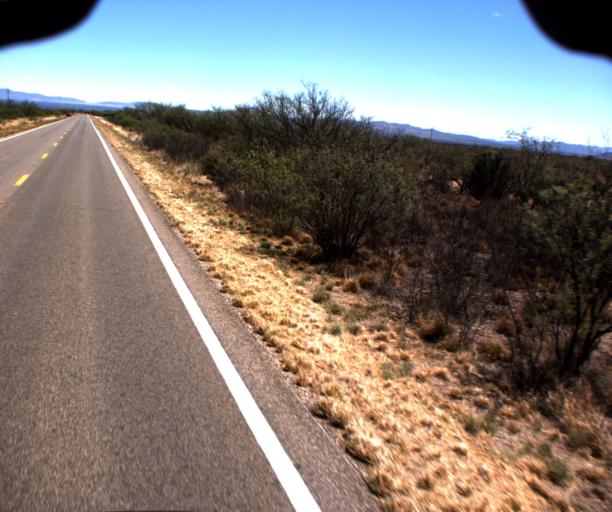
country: US
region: Arizona
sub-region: Cochise County
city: Huachuca City
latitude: 31.7125
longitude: -110.2600
